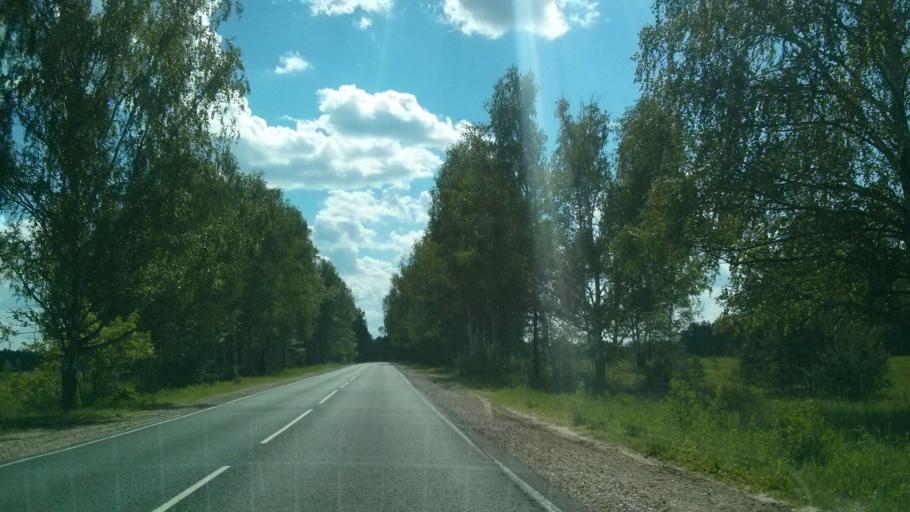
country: RU
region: Vladimir
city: Murom
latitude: 55.5189
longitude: 41.9337
